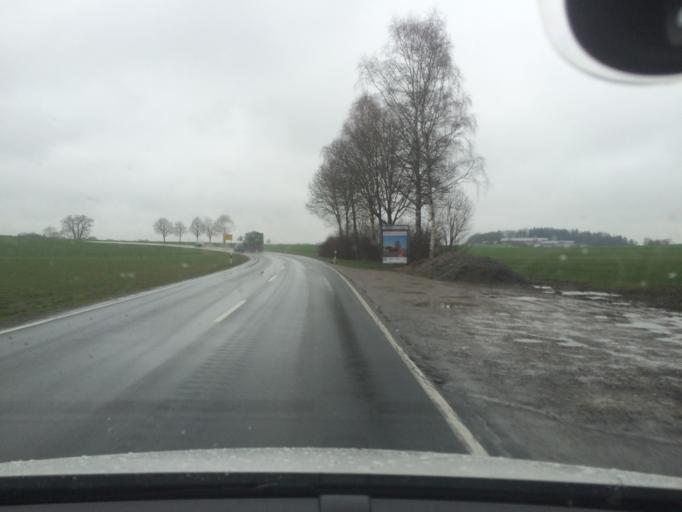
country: DE
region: Bavaria
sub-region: Upper Bavaria
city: Bad Aibling
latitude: 47.8858
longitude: 12.0263
